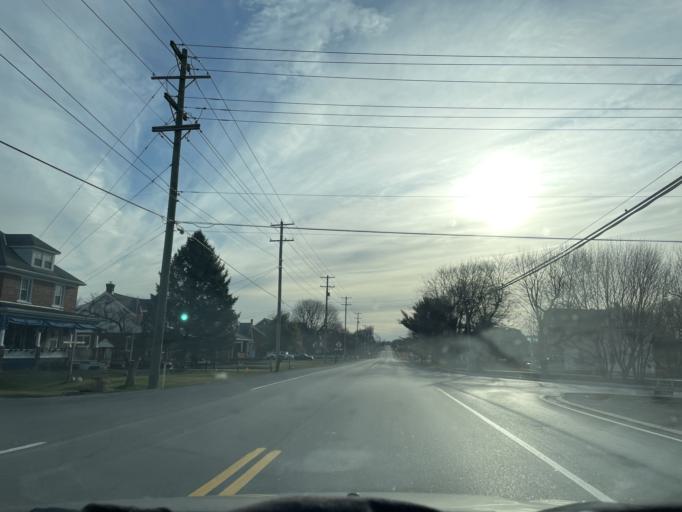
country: US
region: Maryland
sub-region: Washington County
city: Halfway
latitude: 39.6495
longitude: -77.7662
